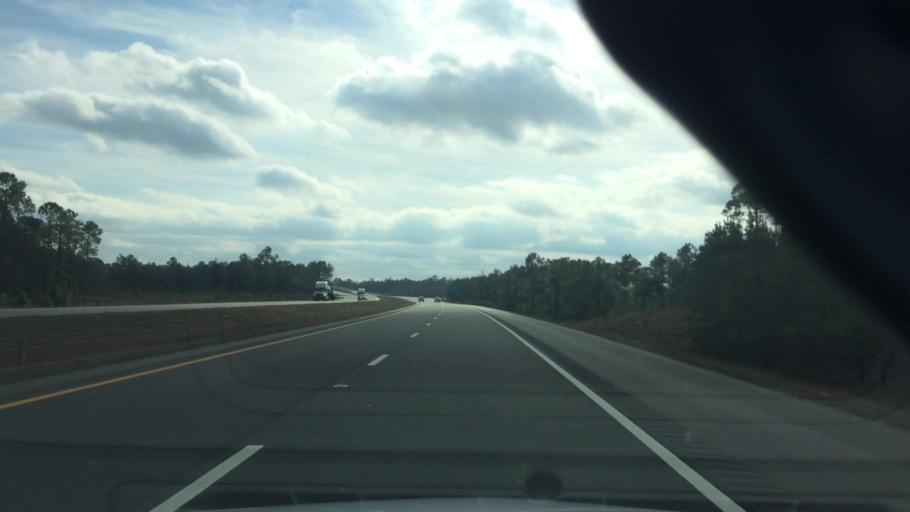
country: US
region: North Carolina
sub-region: Brunswick County
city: Leland
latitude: 34.2675
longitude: -78.0785
